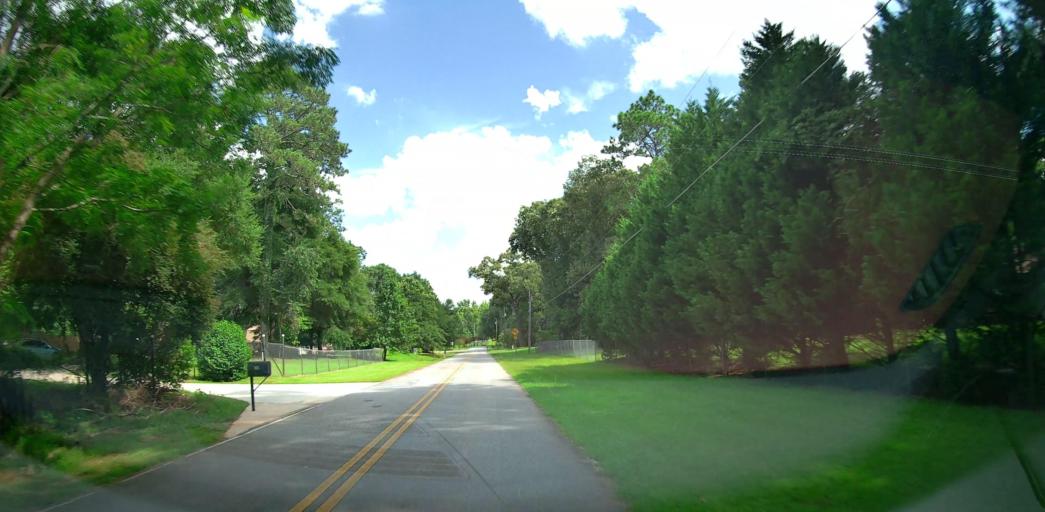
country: US
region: Georgia
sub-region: Houston County
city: Centerville
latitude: 32.5786
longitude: -83.6649
